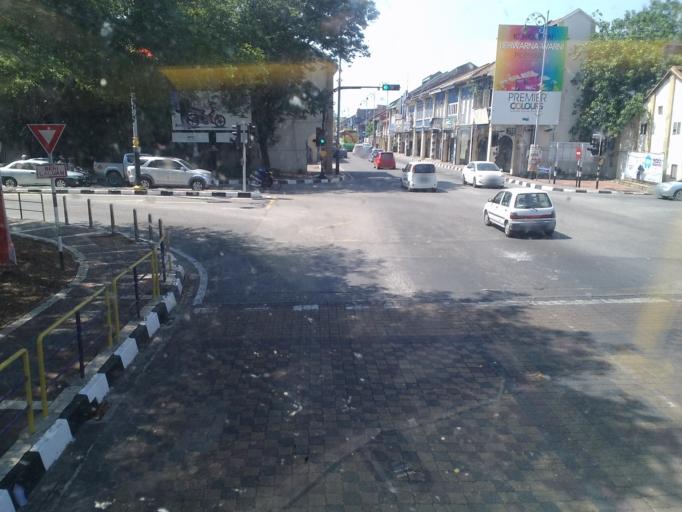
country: MY
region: Kedah
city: Alor Setar
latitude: 6.1186
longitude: 100.3651
